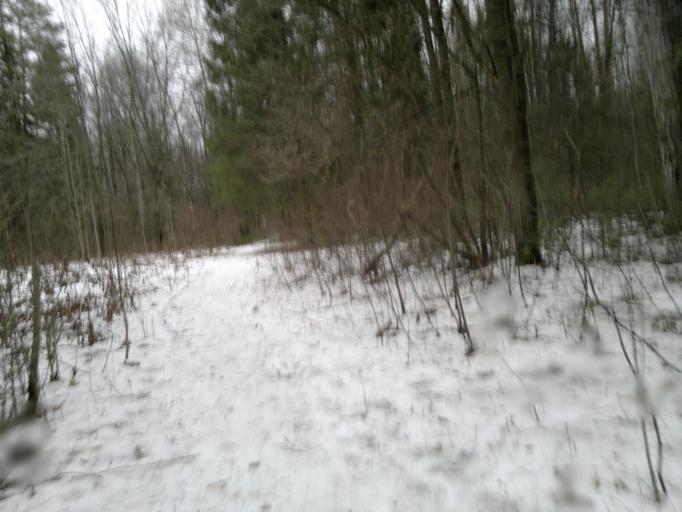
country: RU
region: Mariy-El
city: Yoshkar-Ola
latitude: 56.6118
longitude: 47.9378
